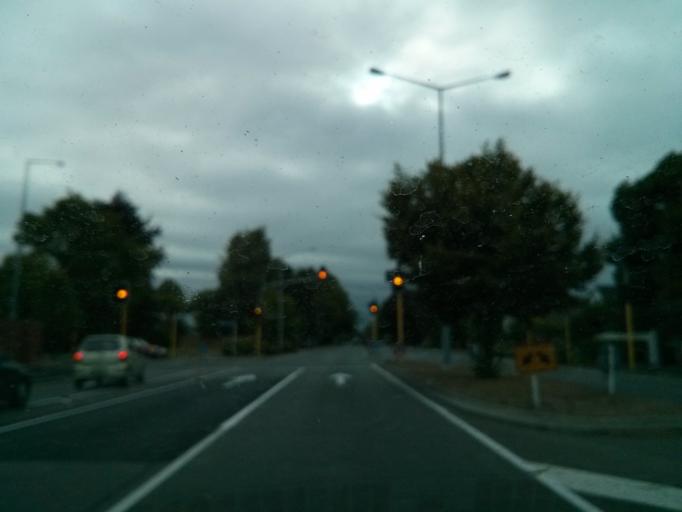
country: NZ
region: Canterbury
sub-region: Christchurch City
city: Christchurch
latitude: -43.5188
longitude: 172.5938
